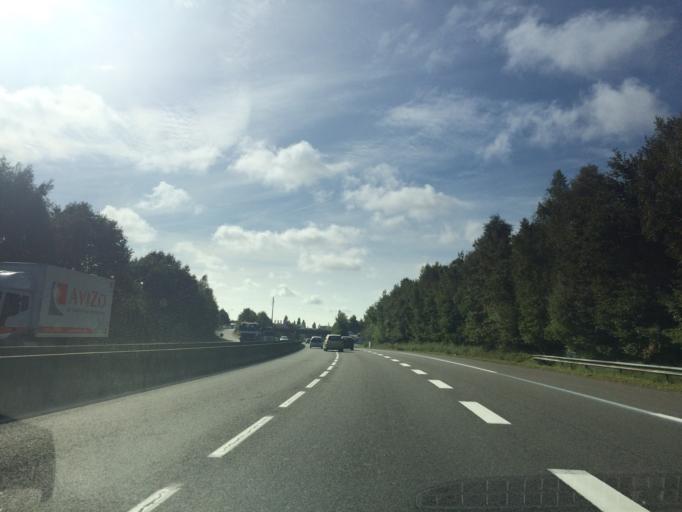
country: FR
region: Pays de la Loire
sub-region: Departement de la Loire-Atlantique
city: Orvault
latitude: 47.2549
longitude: -1.6223
